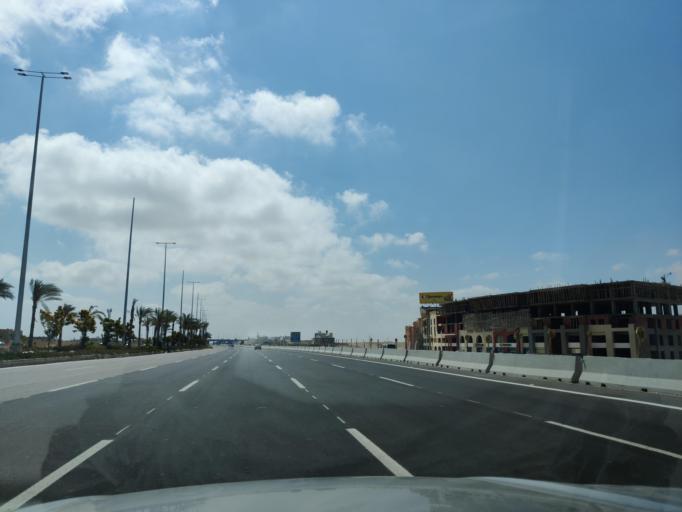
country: EG
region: Muhafazat Matruh
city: Al `Alamayn
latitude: 30.8280
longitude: 28.9743
